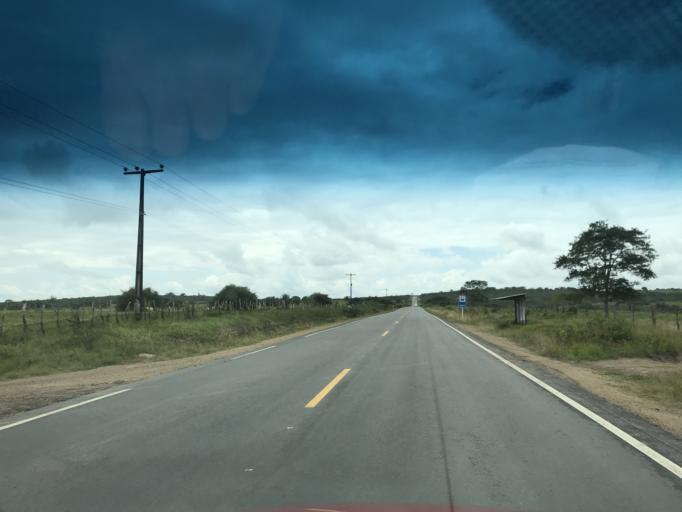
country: BR
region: Bahia
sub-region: Conceicao Do Almeida
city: Conceicao do Almeida
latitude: -12.6733
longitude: -39.2933
